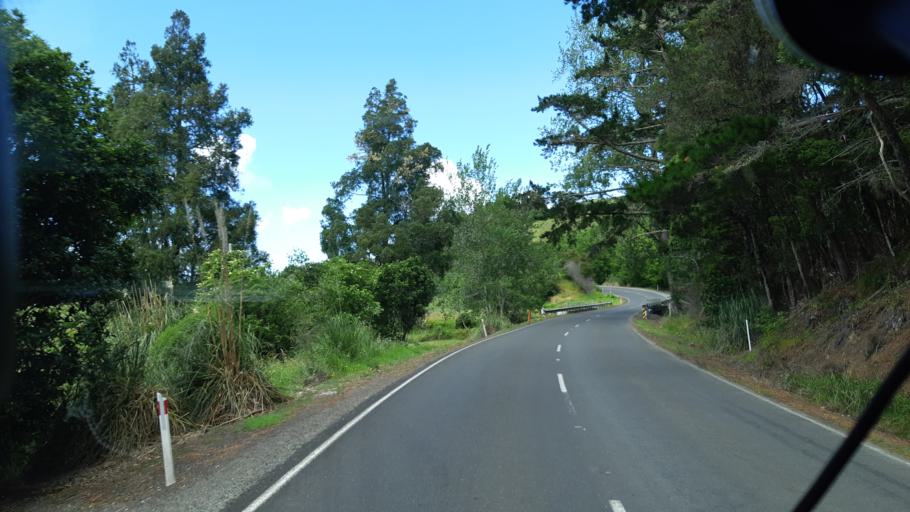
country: NZ
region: Northland
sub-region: Far North District
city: Taipa
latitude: -35.2607
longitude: 173.5274
